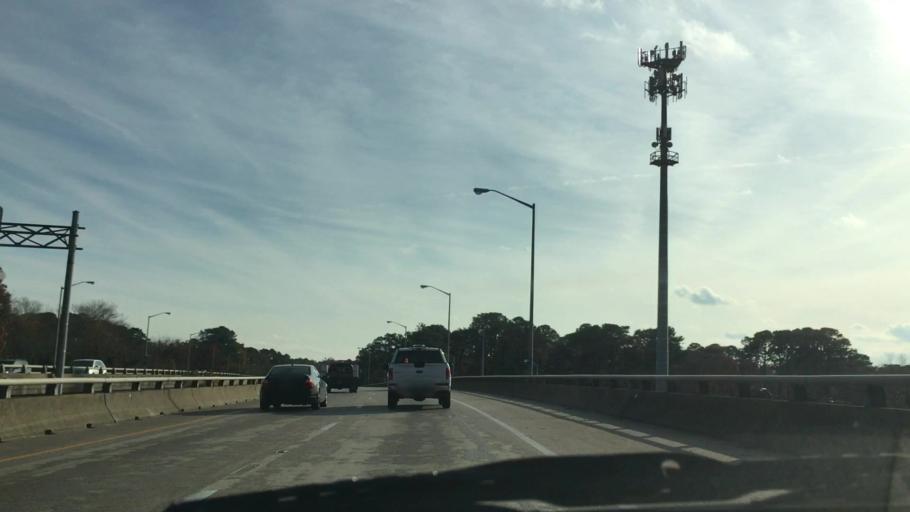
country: US
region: Virginia
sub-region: City of Norfolk
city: Norfolk
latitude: 36.9440
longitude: -76.2668
